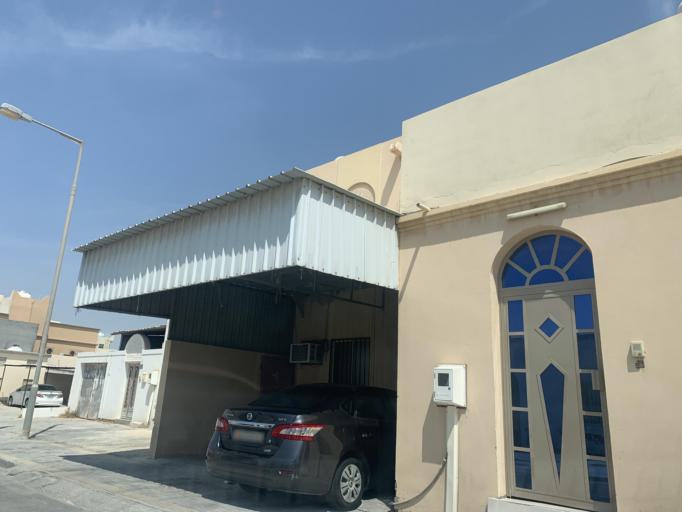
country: BH
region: Central Governorate
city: Madinat Hamad
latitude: 26.1351
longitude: 50.5002
